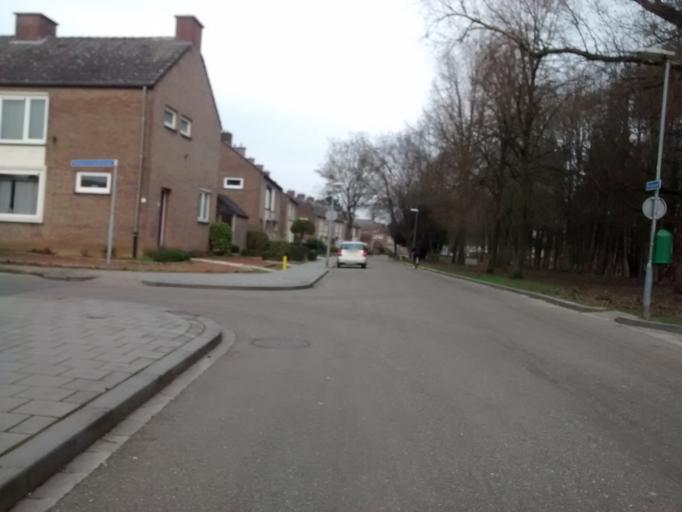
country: NL
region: Limburg
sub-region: Gemeente Voerendaal
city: Kunrade
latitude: 50.8782
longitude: 5.9250
